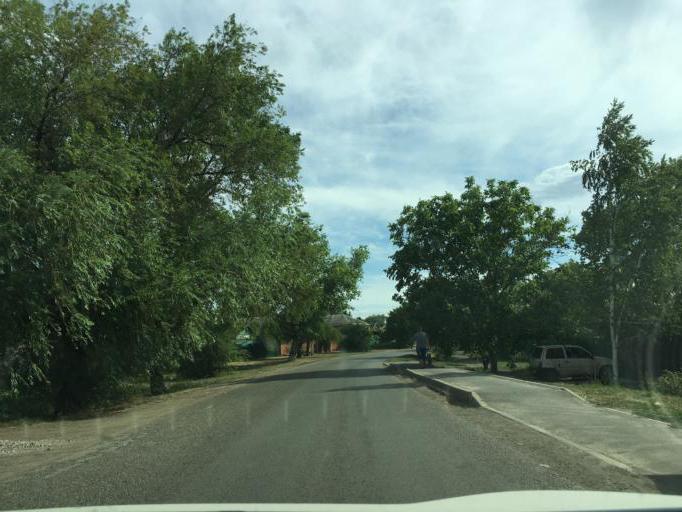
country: RU
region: Krasnodarskiy
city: Kushchevskaya
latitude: 46.5553
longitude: 39.6281
